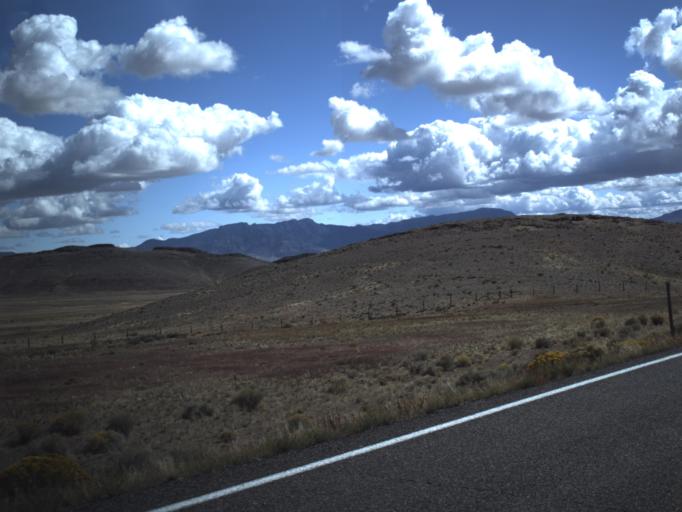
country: US
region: Utah
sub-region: Beaver County
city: Milford
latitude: 38.6123
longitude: -113.8374
